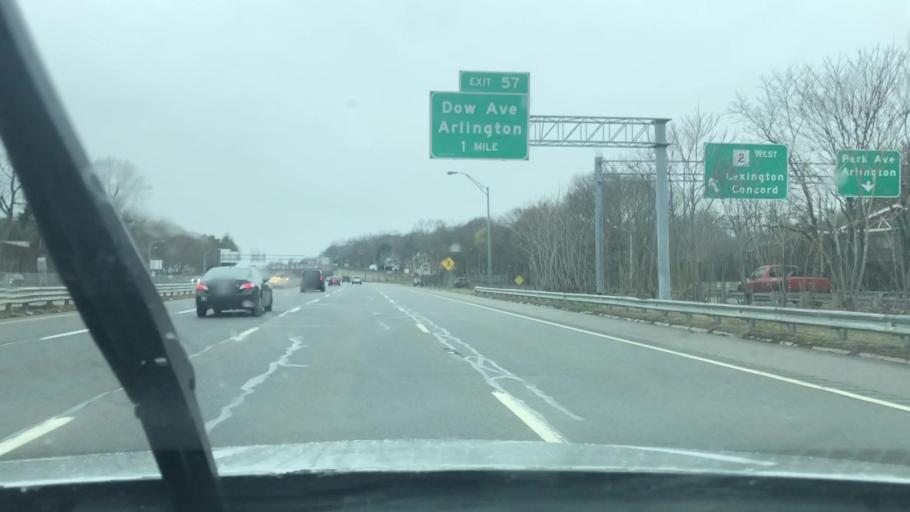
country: US
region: Massachusetts
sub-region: Middlesex County
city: Belmont
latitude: 42.4080
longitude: -71.1700
